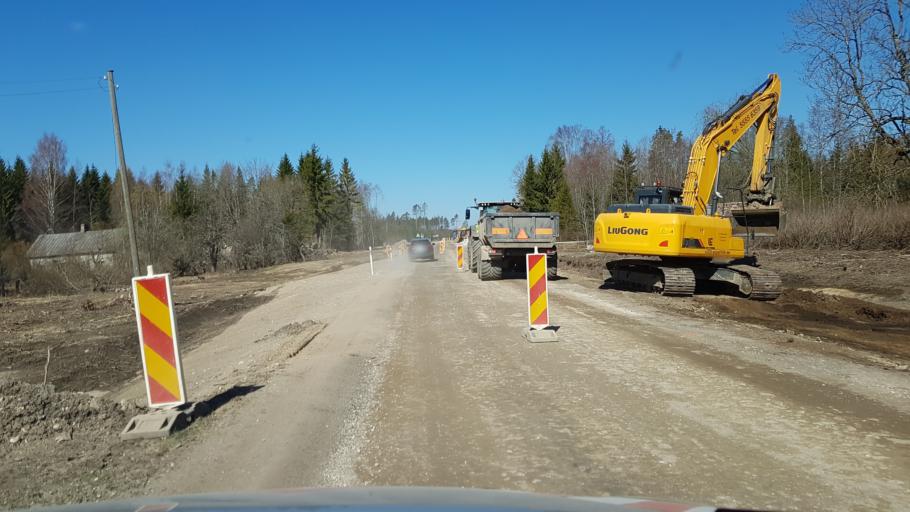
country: EE
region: Jogevamaa
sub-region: Mustvee linn
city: Mustvee
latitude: 59.0418
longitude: 26.6652
